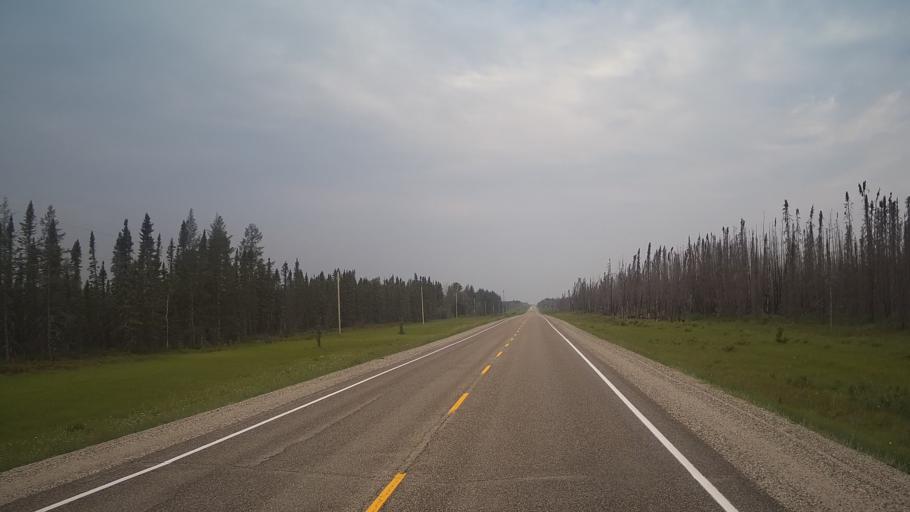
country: CA
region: Ontario
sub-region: Algoma
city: Hornepayne
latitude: 49.7601
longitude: -84.9038
